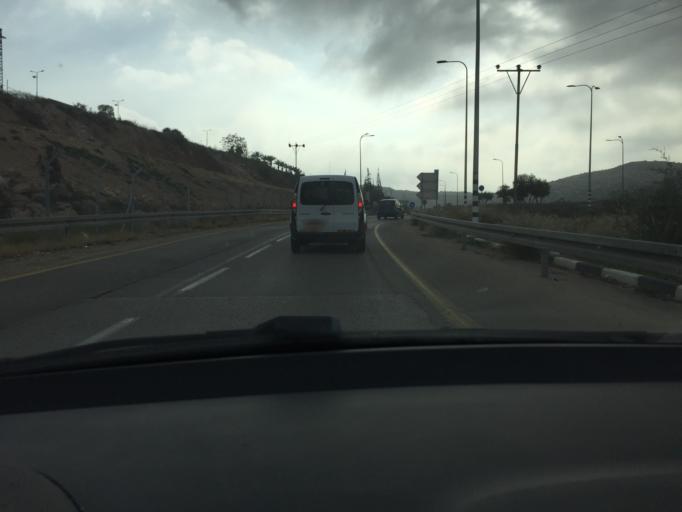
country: PS
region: West Bank
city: Al Lubban al Gharbi
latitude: 32.0338
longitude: 35.0479
